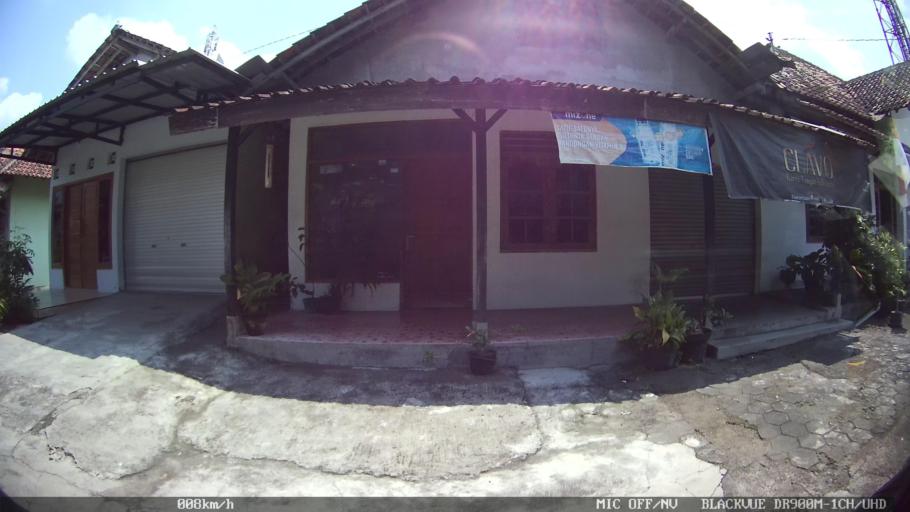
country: ID
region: Daerah Istimewa Yogyakarta
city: Depok
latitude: -7.8127
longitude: 110.4079
